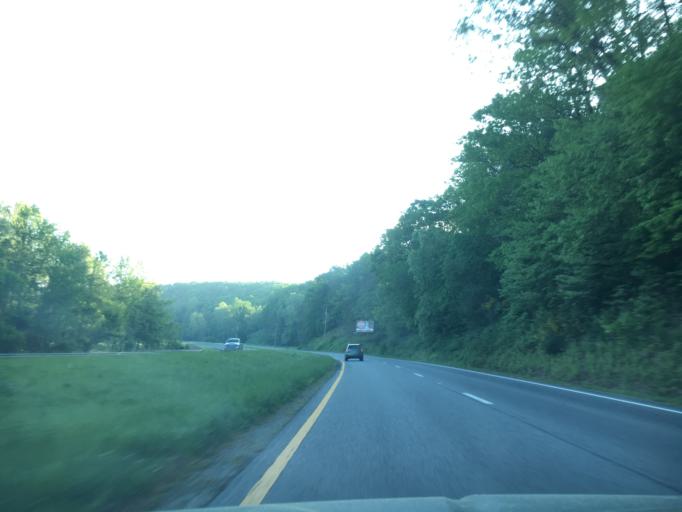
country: US
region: Virginia
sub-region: Campbell County
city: Rustburg
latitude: 37.3140
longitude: -79.1054
